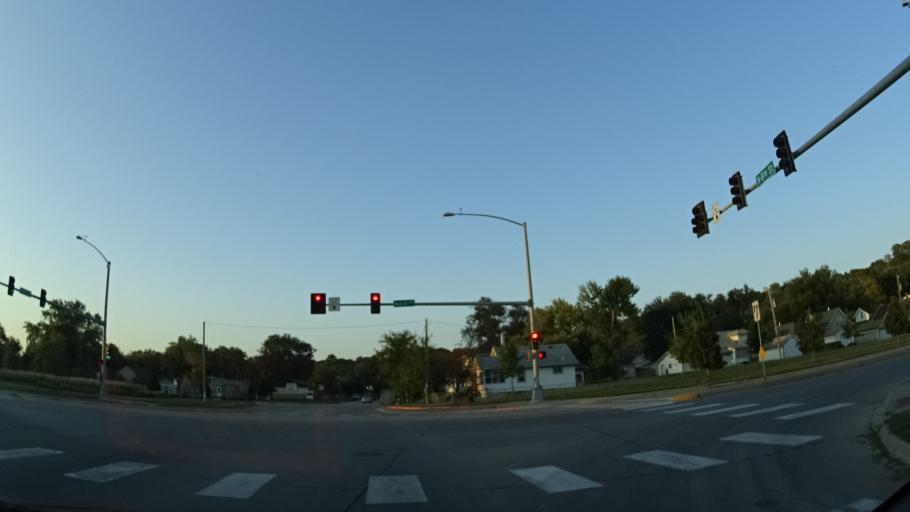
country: US
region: Iowa
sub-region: Pottawattamie County
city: Council Bluffs
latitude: 41.2678
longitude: -95.8560
